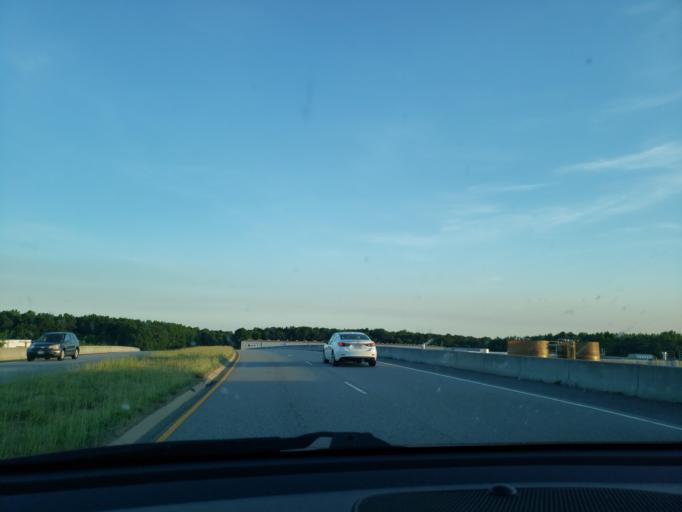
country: US
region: Virginia
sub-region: Henrico County
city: Fort Lee
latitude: 37.4960
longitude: -77.3412
